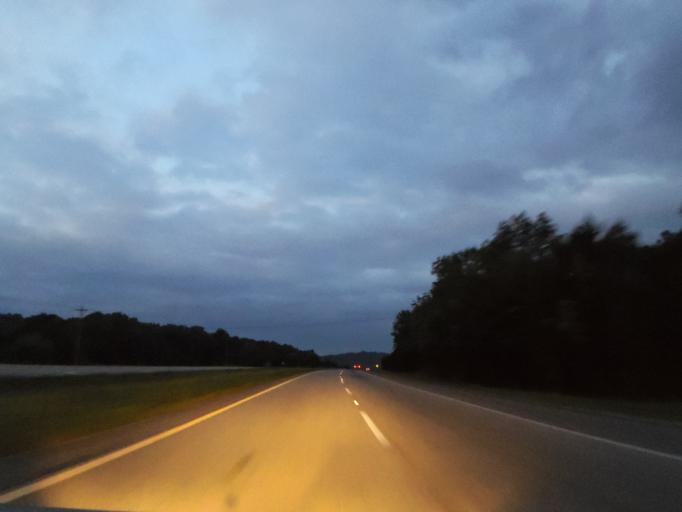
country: US
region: Alabama
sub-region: Madison County
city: New Hope
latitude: 34.6129
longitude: -86.2411
